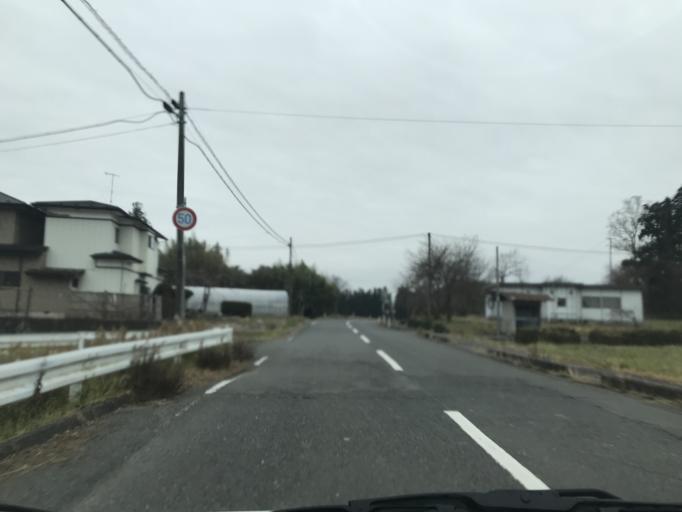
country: JP
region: Iwate
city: Ichinoseki
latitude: 38.7420
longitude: 141.2189
